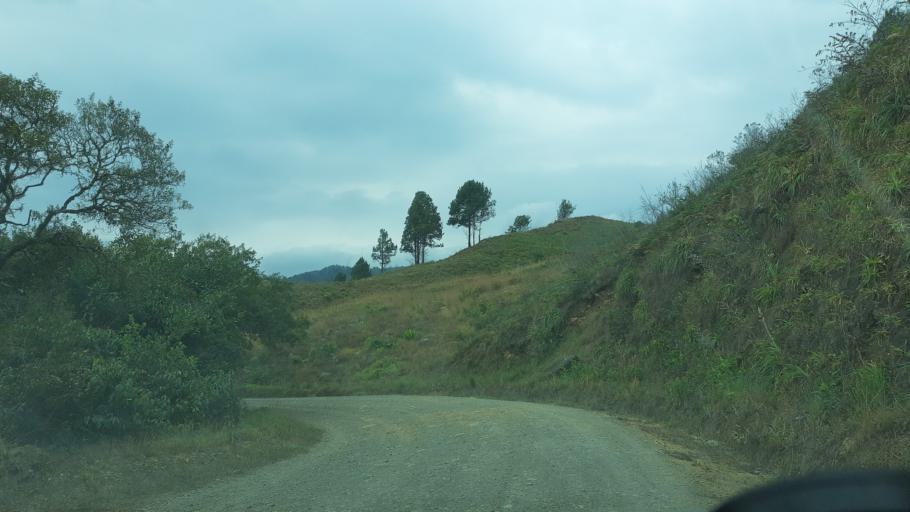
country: CO
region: Boyaca
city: Somondoco
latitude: 4.9840
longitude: -73.3753
